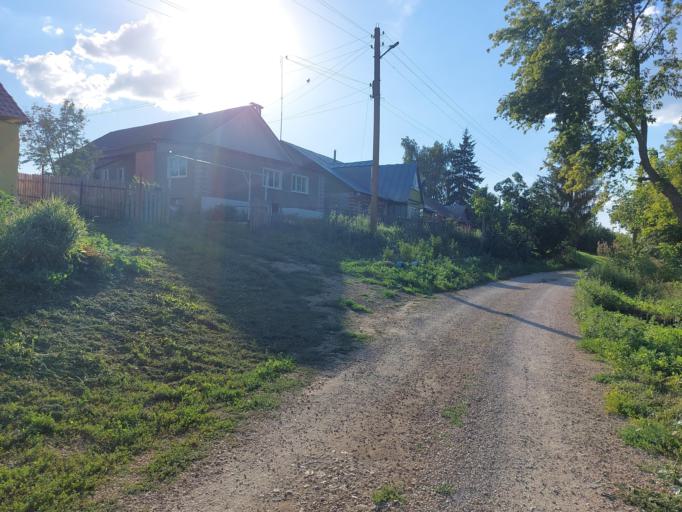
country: RU
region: Lipetsk
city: Terbuny
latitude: 52.2768
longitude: 38.1919
